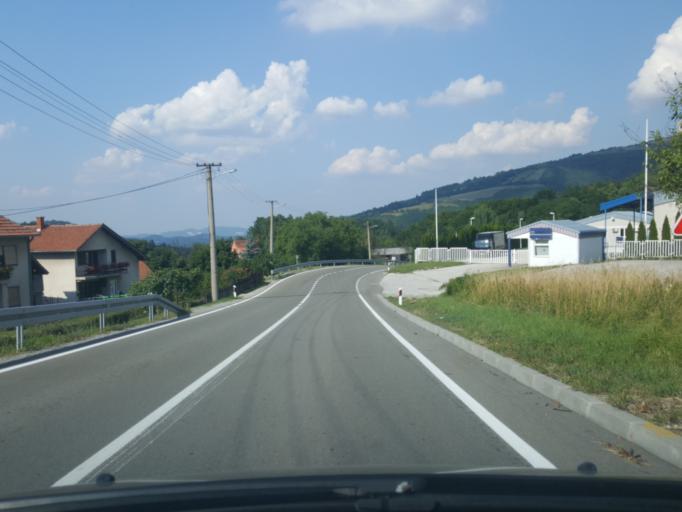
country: RS
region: Central Serbia
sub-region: Moravicki Okrug
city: Gornji Milanovac
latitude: 44.1419
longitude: 20.4973
